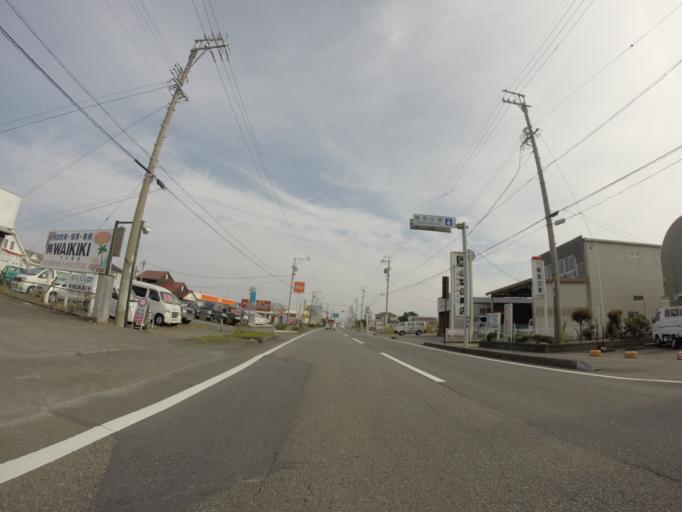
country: JP
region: Shizuoka
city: Sagara
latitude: 34.7346
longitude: 138.2273
